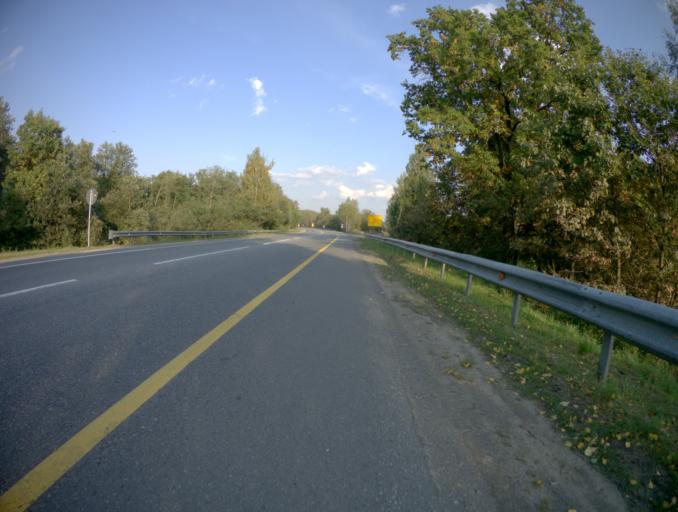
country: RU
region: Vladimir
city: Kameshkovo
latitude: 56.1956
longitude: 40.8858
